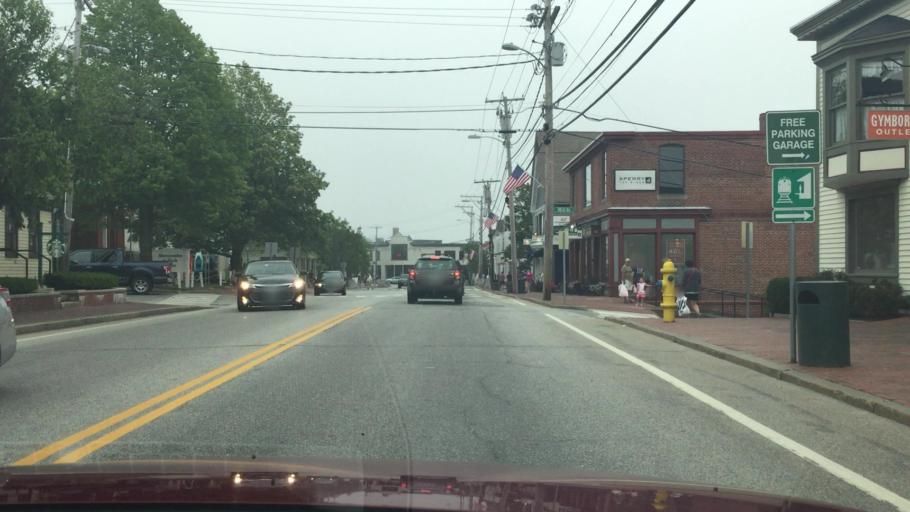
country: US
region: Maine
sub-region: Cumberland County
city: Freeport
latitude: 43.8563
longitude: -70.1045
